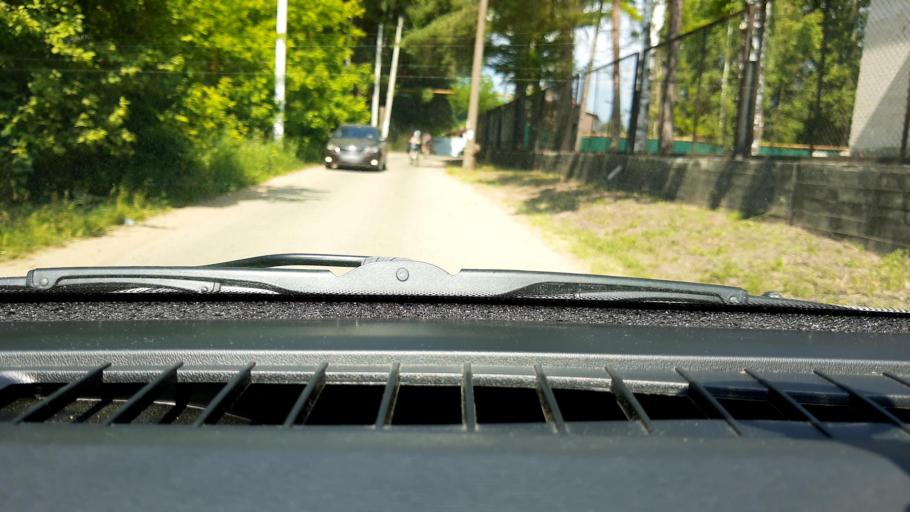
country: RU
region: Nizjnij Novgorod
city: Burevestnik
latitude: 56.1957
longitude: 43.7736
